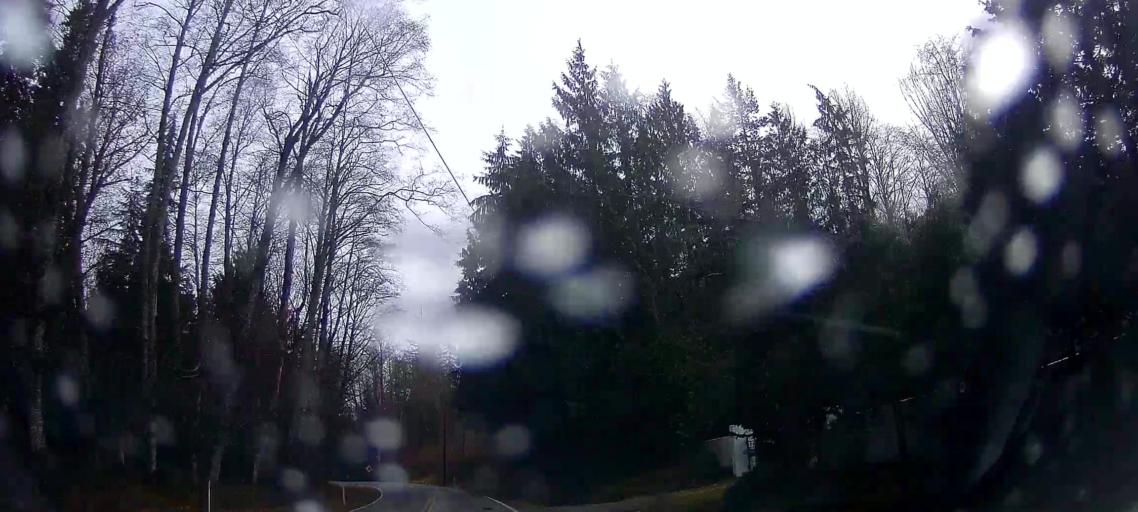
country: US
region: Washington
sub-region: Skagit County
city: Clear Lake
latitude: 48.4767
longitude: -122.1610
